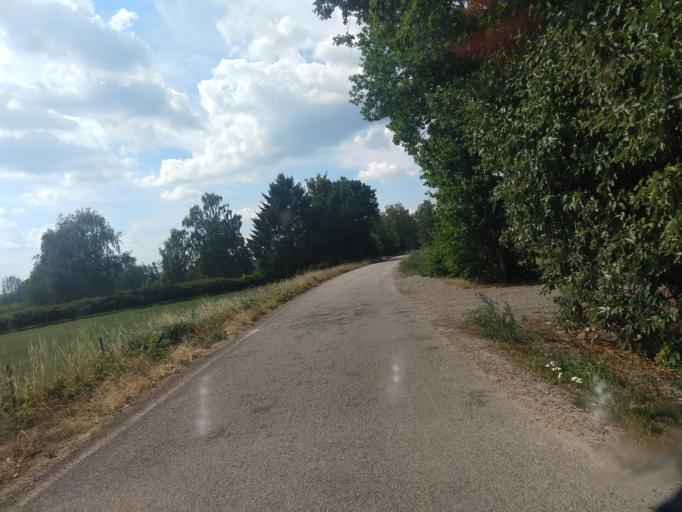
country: SE
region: Blekinge
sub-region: Karlskrona Kommun
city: Nattraby
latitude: 56.2462
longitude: 15.5400
